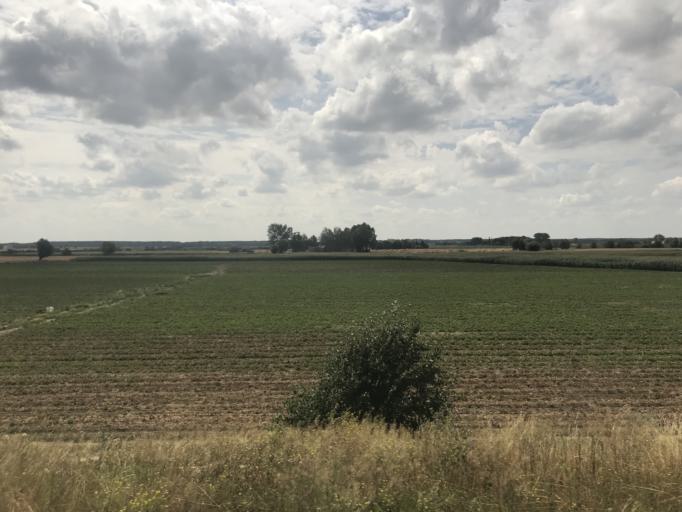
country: PL
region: Greater Poland Voivodeship
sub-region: Powiat poznanski
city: Pobiedziska
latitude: 52.4871
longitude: 17.3312
